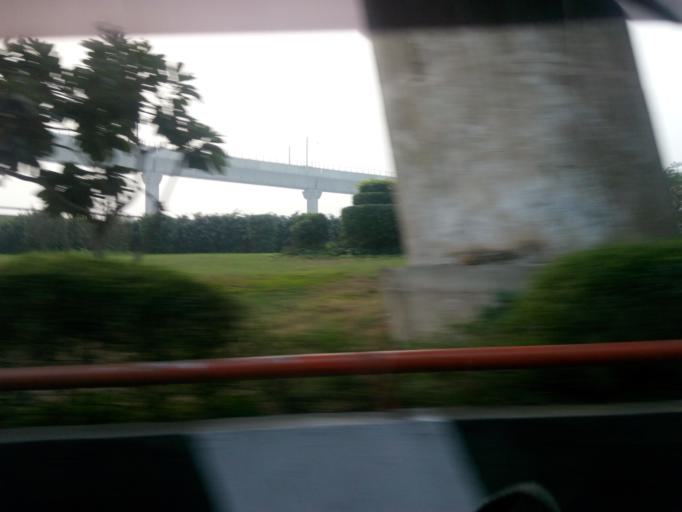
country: IN
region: NCT
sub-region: Central Delhi
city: Karol Bagh
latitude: 28.5955
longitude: 77.1664
